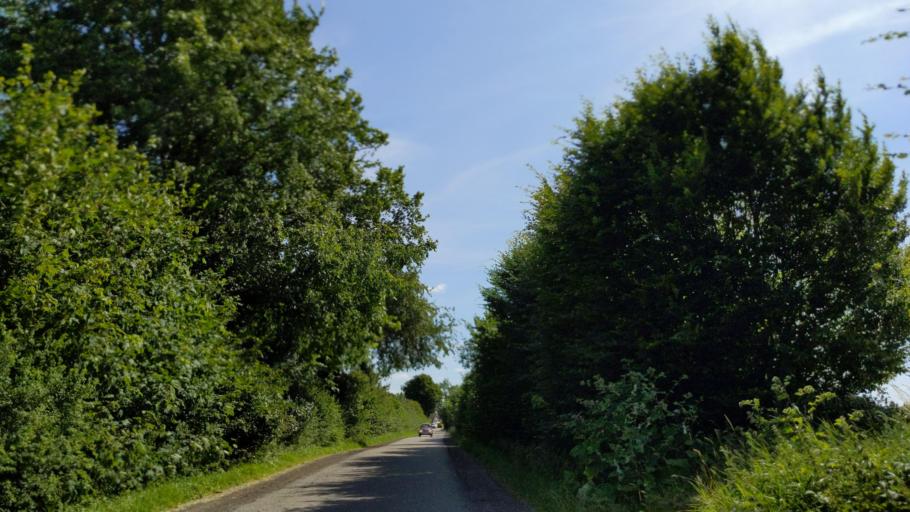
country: DE
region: Schleswig-Holstein
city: Altenkrempe
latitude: 54.1451
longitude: 10.8248
